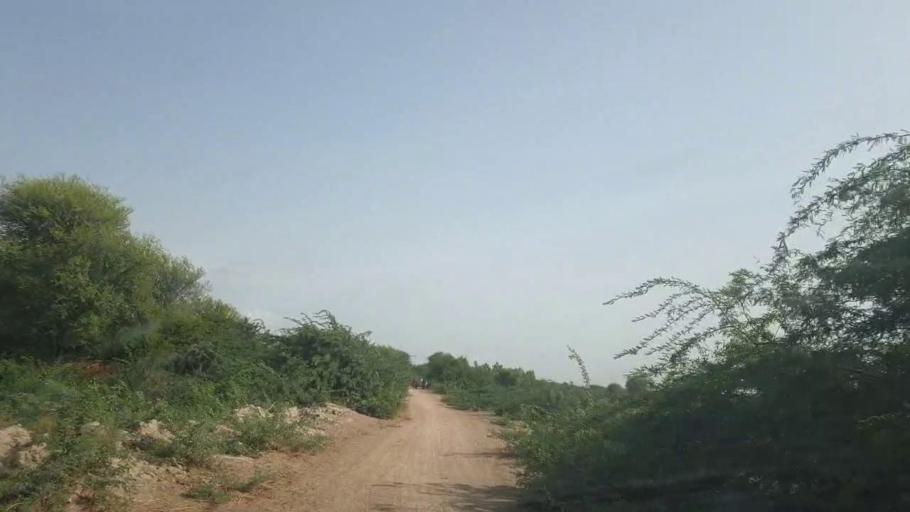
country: PK
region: Sindh
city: Tando Bago
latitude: 24.8068
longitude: 69.1866
